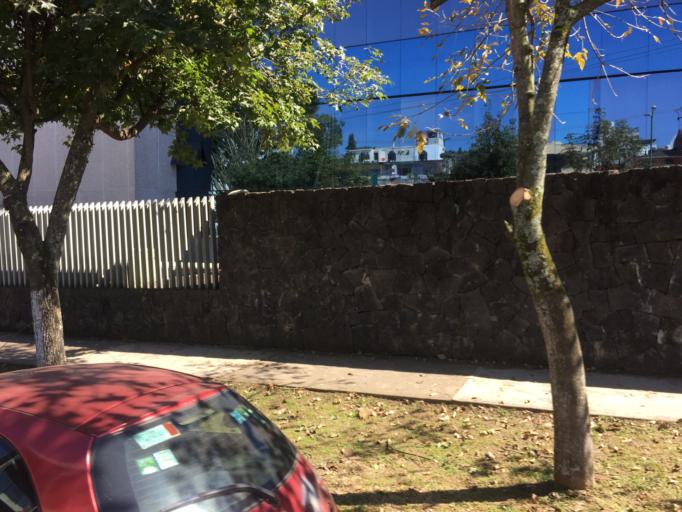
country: MX
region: Veracruz
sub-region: Xalapa
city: Xalapa de Enriquez
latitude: 19.5389
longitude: -96.9089
